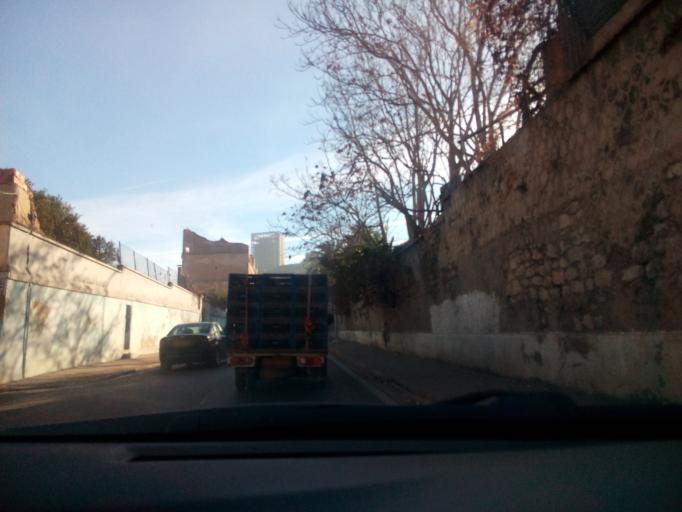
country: DZ
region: Oran
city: Oran
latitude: 35.7074
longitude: -0.6553
